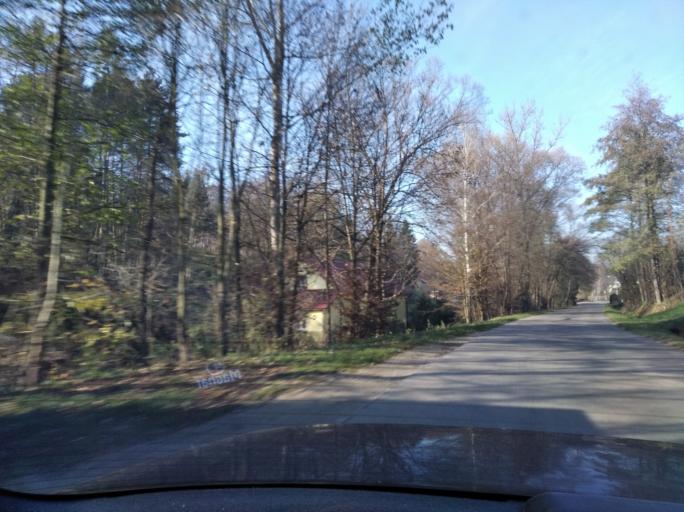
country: PL
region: Subcarpathian Voivodeship
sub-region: Powiat strzyzowski
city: Frysztak
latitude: 49.8764
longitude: 21.6174
